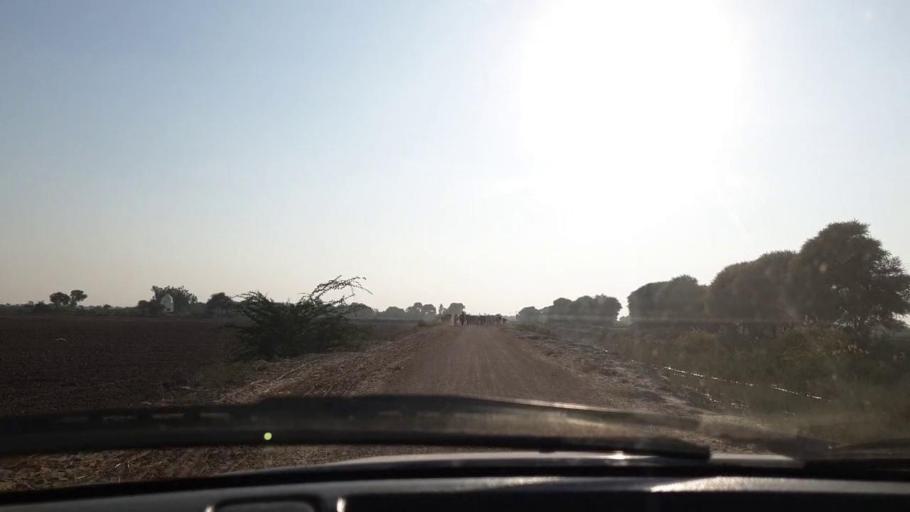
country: PK
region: Sindh
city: Bulri
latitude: 24.8067
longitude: 68.3956
